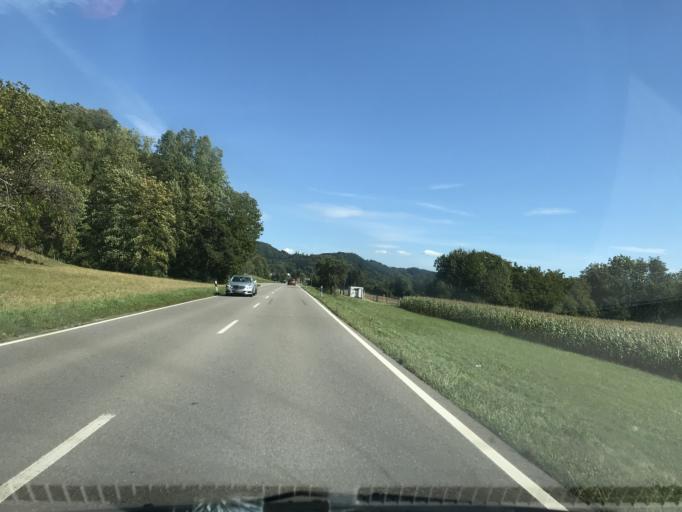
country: DE
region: Baden-Wuerttemberg
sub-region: Freiburg Region
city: Schworstadt
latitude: 47.5890
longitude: 7.8966
